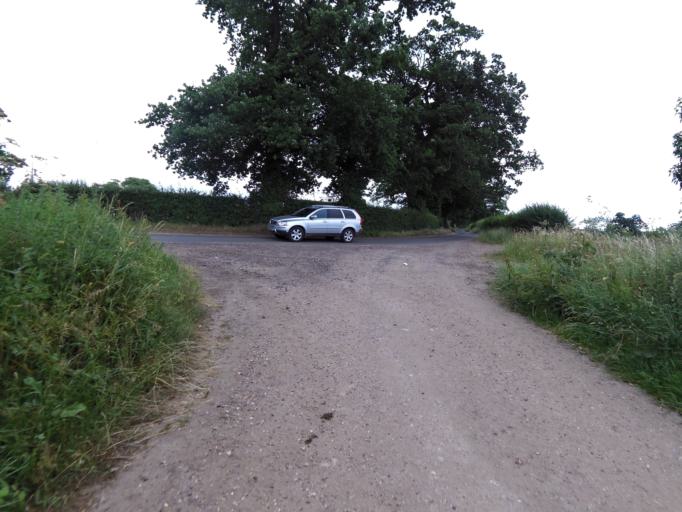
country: GB
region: England
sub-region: Norfolk
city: Diss
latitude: 52.3840
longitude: 1.1500
